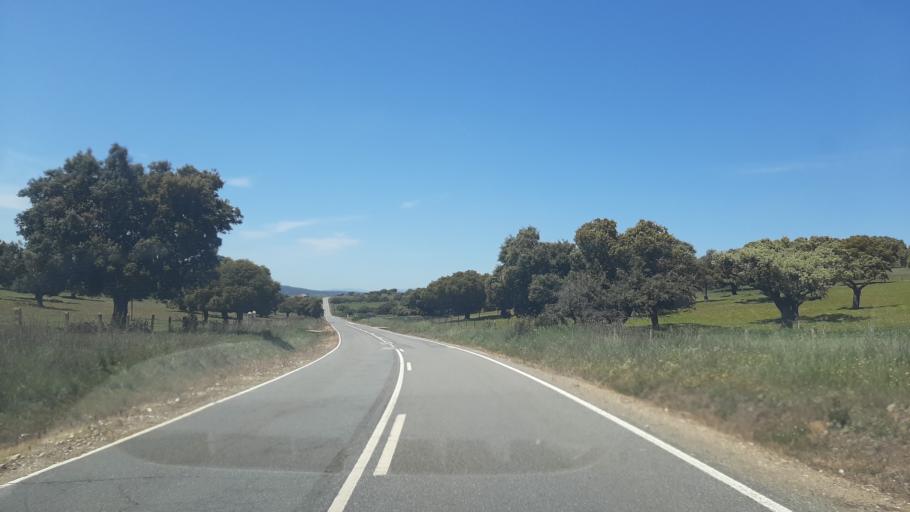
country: ES
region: Castille and Leon
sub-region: Provincia de Salamanca
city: Puente del Congosto
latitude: 40.5357
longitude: -5.5460
